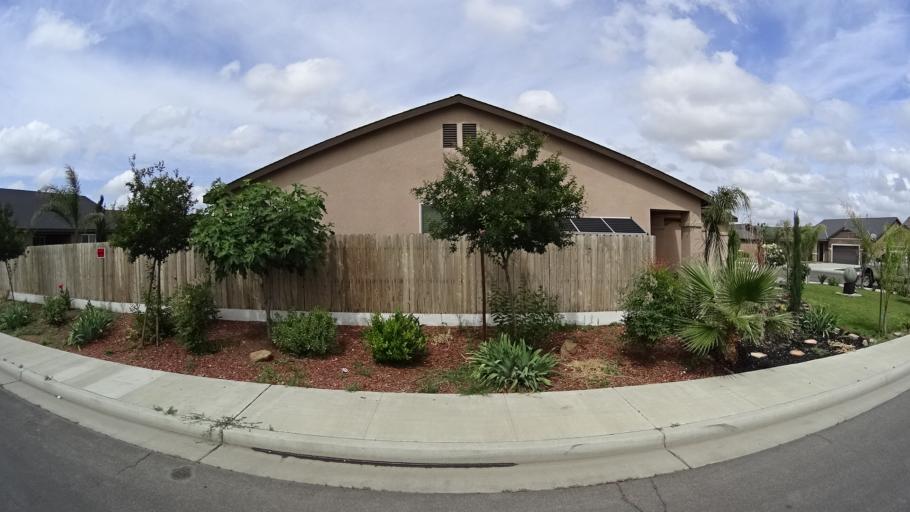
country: US
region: California
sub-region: Kings County
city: Hanford
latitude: 36.3082
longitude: -119.6644
